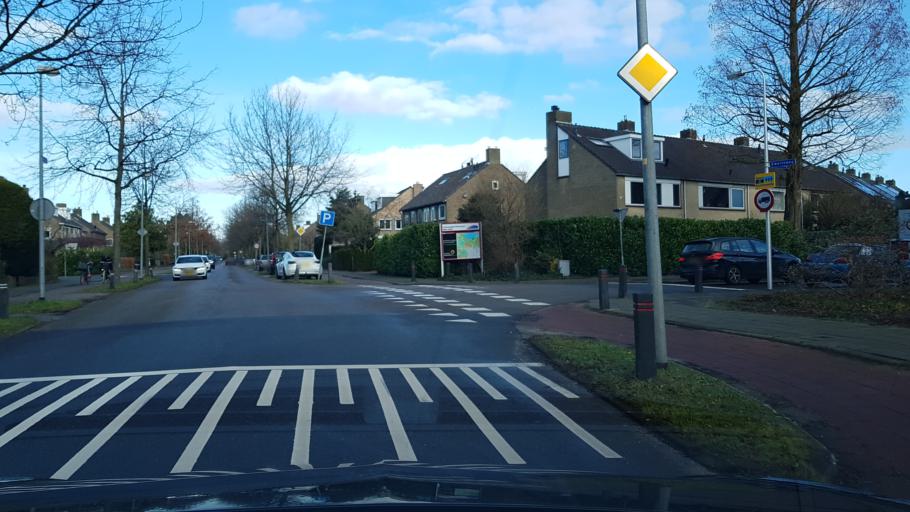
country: NL
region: North Holland
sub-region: Gemeente Bussum
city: Bussum
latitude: 52.2791
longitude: 5.1476
